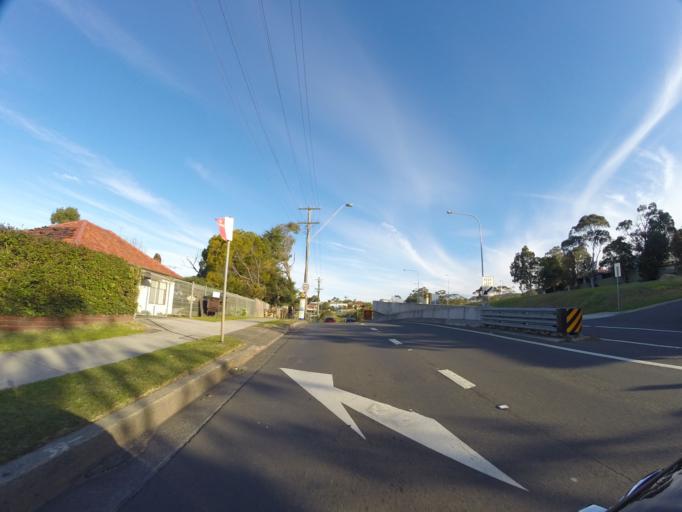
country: AU
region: New South Wales
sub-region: Wollongong
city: Bulli
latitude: -34.3219
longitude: 150.9137
